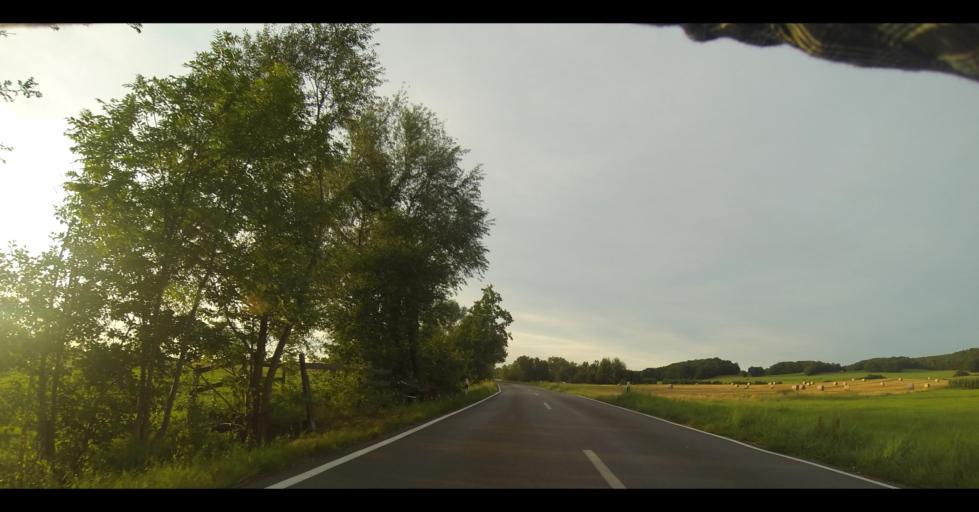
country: DE
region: Saxony
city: Moritzburg
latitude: 51.1524
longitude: 13.7324
